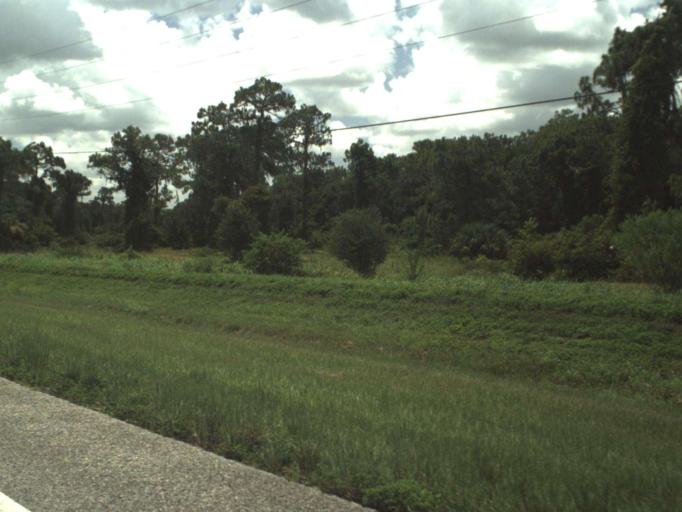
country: US
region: Florida
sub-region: Indian River County
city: Fellsmere
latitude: 27.6810
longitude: -80.8306
